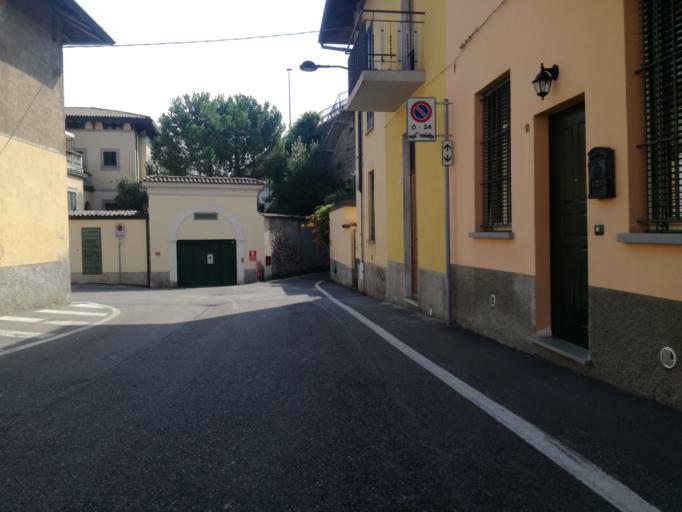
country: IT
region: Lombardy
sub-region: Provincia di Bergamo
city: Capriate San Gervasio
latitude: 45.6102
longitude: 9.5228
